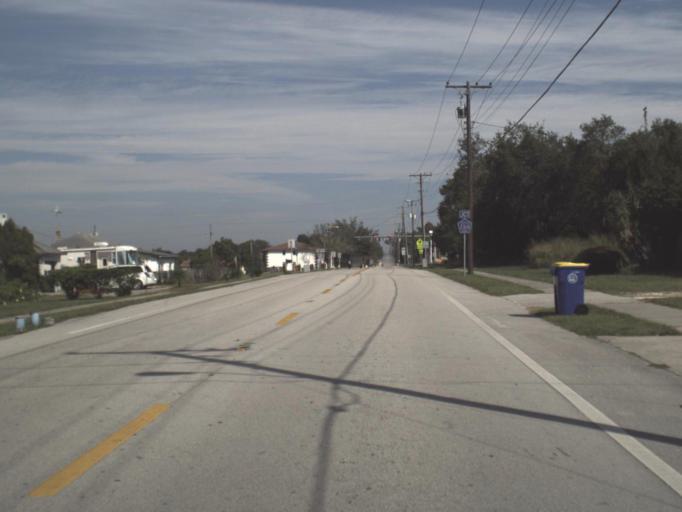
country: US
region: Florida
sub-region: Highlands County
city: Avon Park
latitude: 27.5937
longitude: -81.4940
